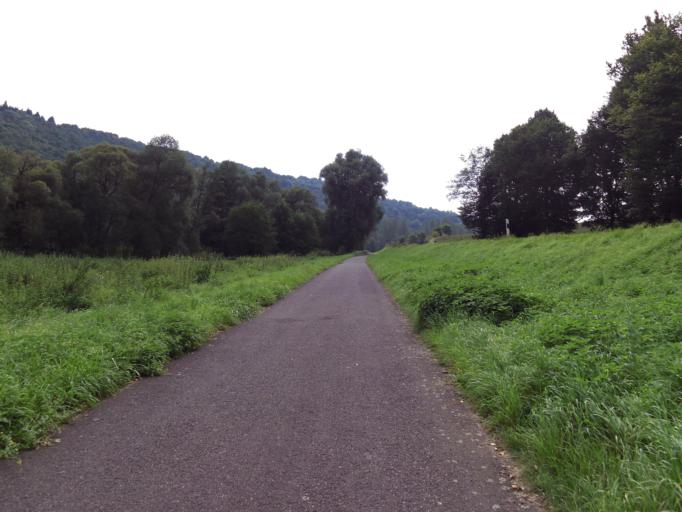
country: DE
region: Rheinland-Pfalz
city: Kalkofen
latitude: 49.7430
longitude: 7.8209
